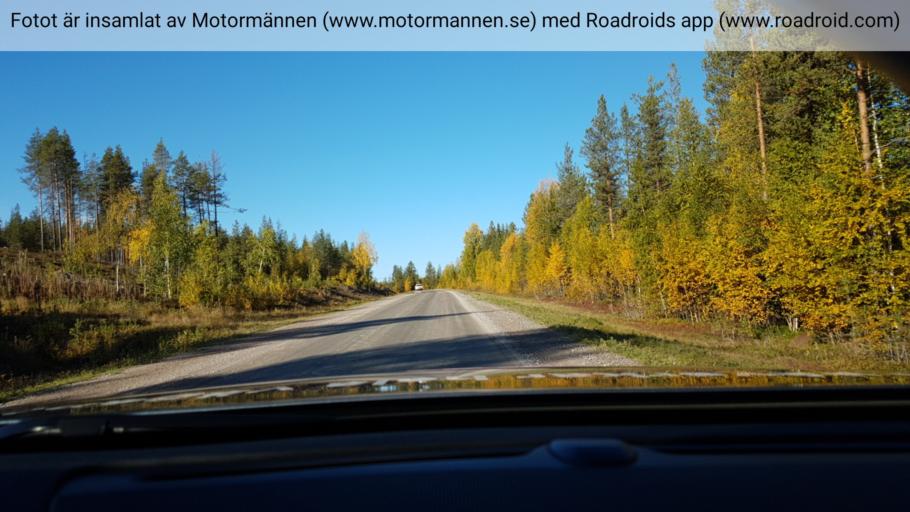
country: SE
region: Norrbotten
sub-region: Alvsbyns Kommun
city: AElvsbyn
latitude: 66.2653
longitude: 21.0649
